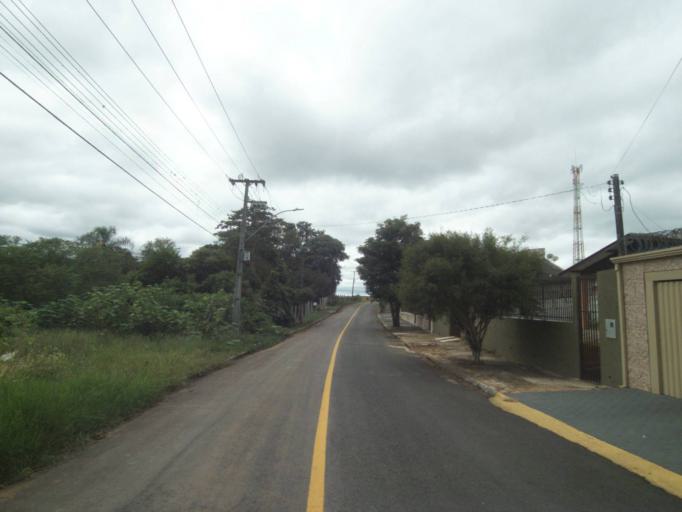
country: BR
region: Parana
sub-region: Telemaco Borba
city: Telemaco Borba
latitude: -24.3313
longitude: -50.6086
